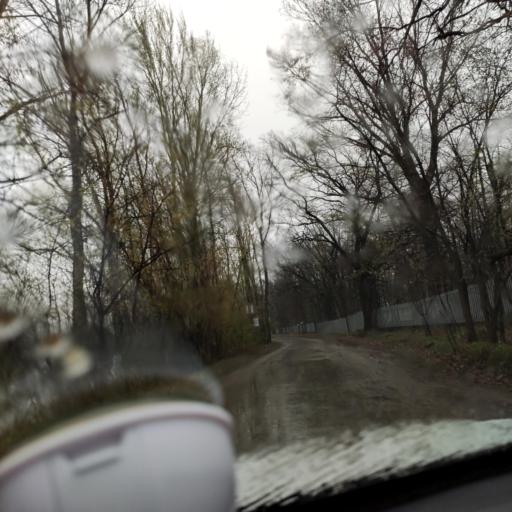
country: RU
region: Samara
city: Novokuybyshevsk
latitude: 53.1400
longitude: 49.9714
